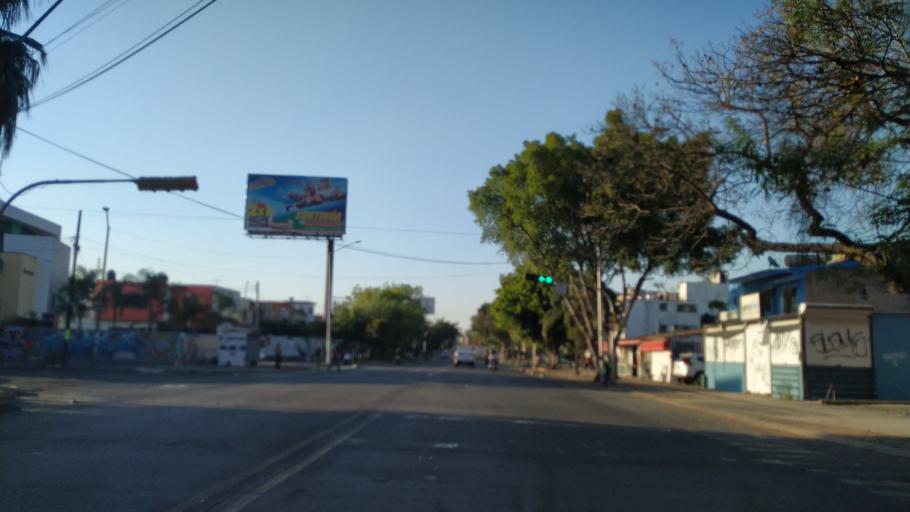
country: MX
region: Jalisco
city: Tlaquepaque
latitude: 20.6579
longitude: -103.3292
